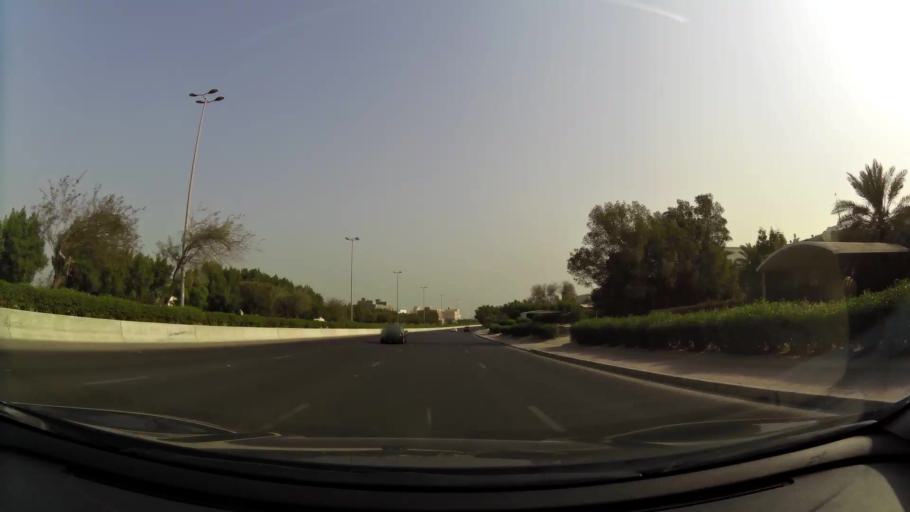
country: KW
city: Al Funaytis
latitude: 29.2232
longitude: 48.0849
